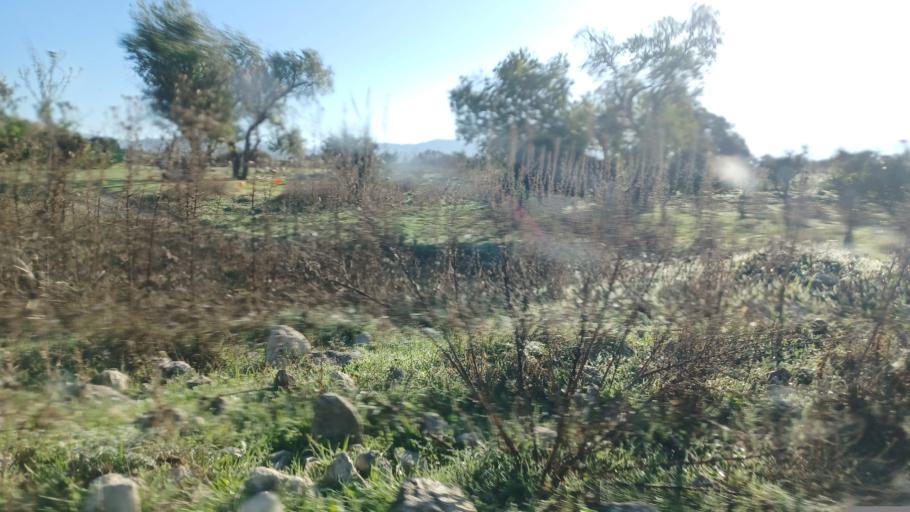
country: CY
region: Pafos
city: Polis
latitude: 34.9766
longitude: 32.5263
